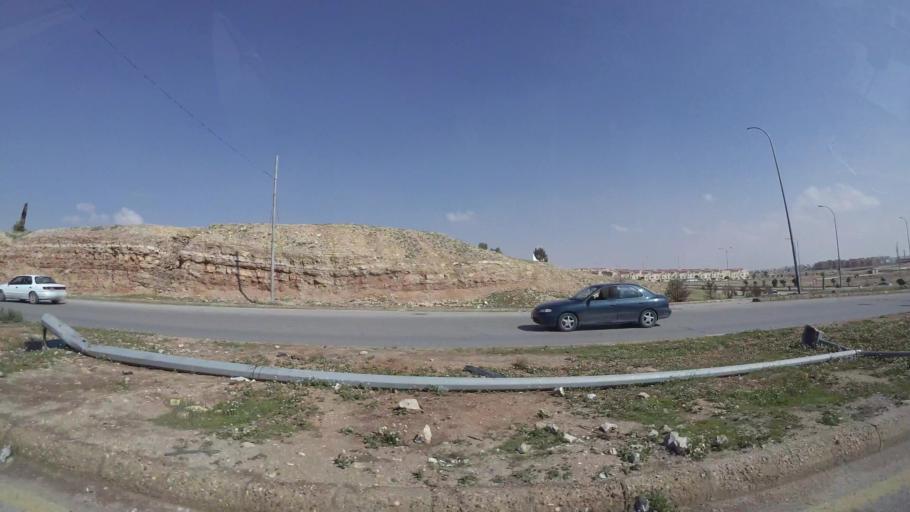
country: JO
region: Zarqa
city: Zarqa
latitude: 32.0734
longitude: 36.1038
